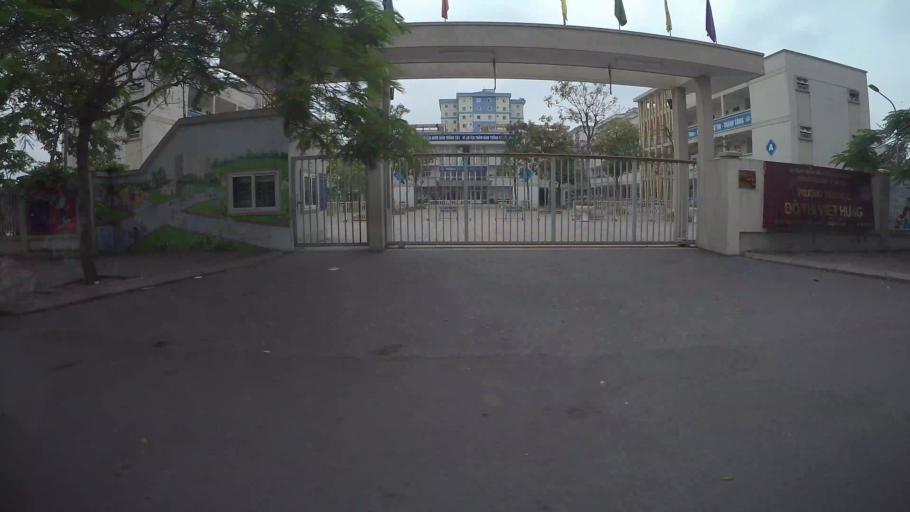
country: VN
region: Ha Noi
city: Trau Quy
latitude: 21.0638
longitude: 105.9107
